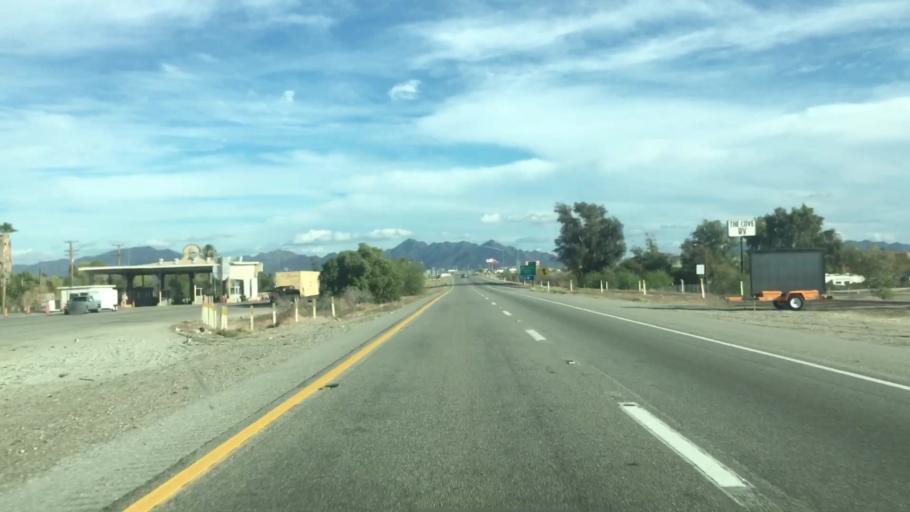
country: US
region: Arizona
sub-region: La Paz County
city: Ehrenberg
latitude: 33.6061
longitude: -114.5371
